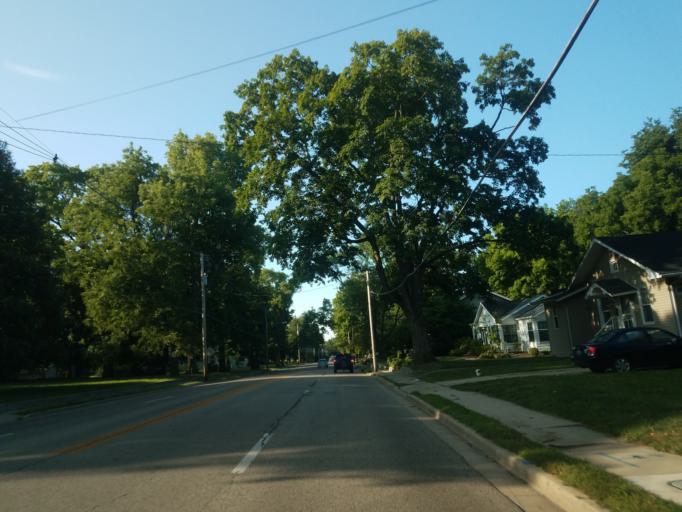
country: US
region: Illinois
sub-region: McLean County
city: Normal
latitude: 40.4991
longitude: -88.9821
